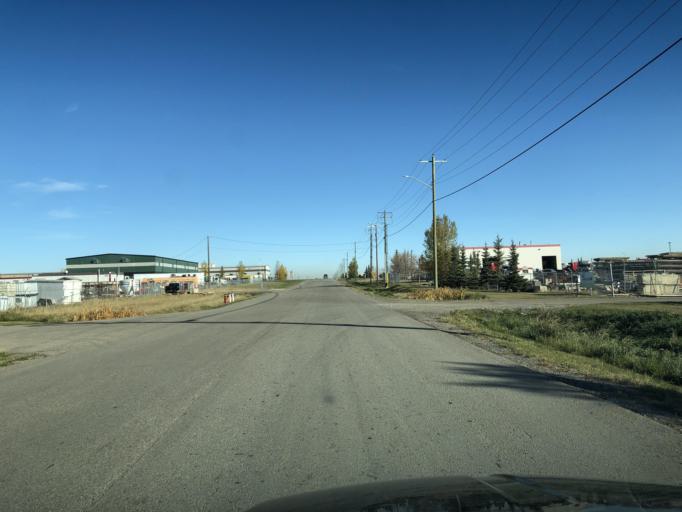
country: CA
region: Alberta
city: Chestermere
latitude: 50.9638
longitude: -113.9026
